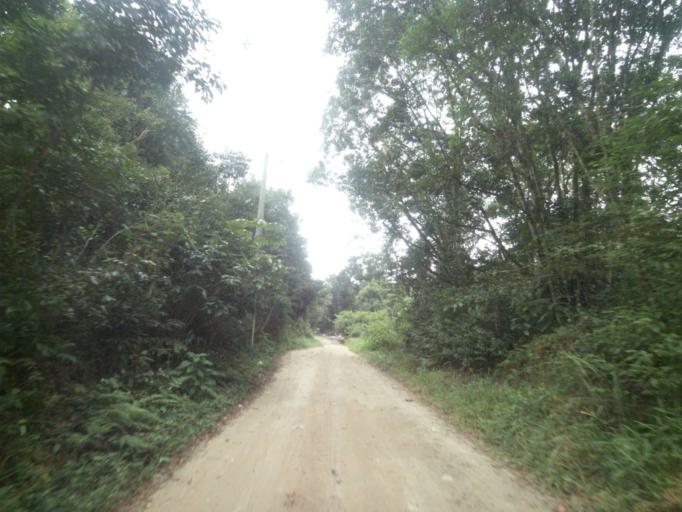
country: BR
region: Parana
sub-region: Paranagua
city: Paranagua
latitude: -25.5404
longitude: -48.5532
